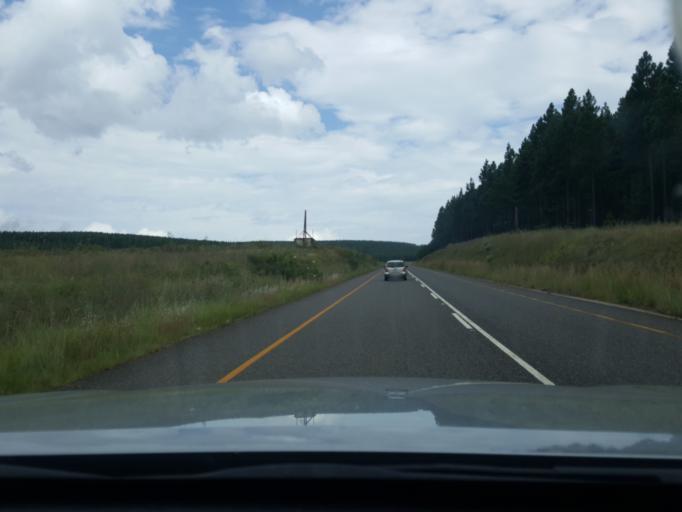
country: ZA
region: Mpumalanga
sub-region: Ehlanzeni District
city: Graksop
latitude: -25.1551
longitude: 30.8332
